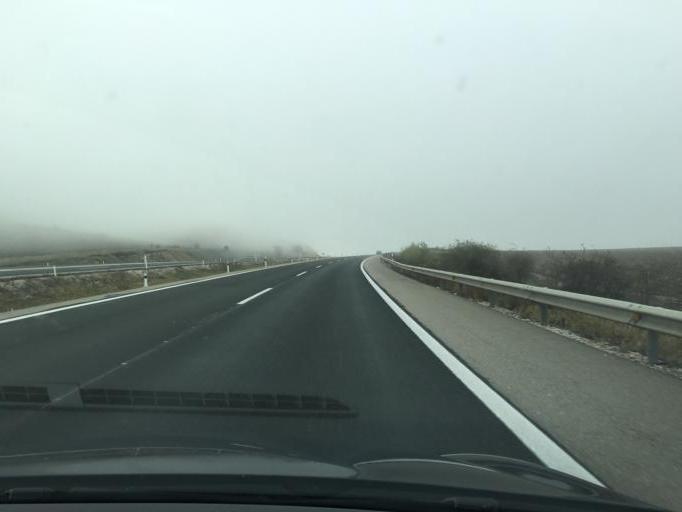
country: ES
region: Castille and Leon
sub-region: Provincia de Burgos
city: Villanueva de Teba
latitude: 42.6238
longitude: -3.1451
